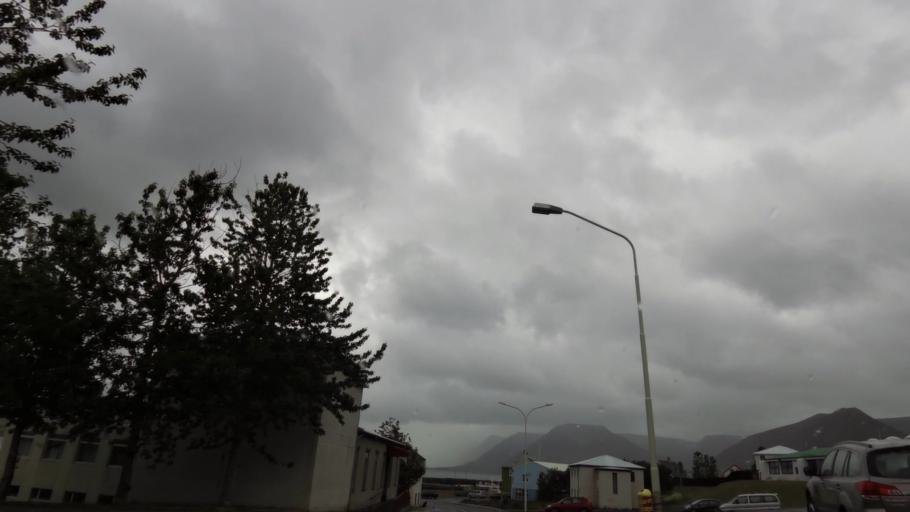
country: IS
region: Westfjords
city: Isafjoerdur
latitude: 65.8776
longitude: -23.4929
